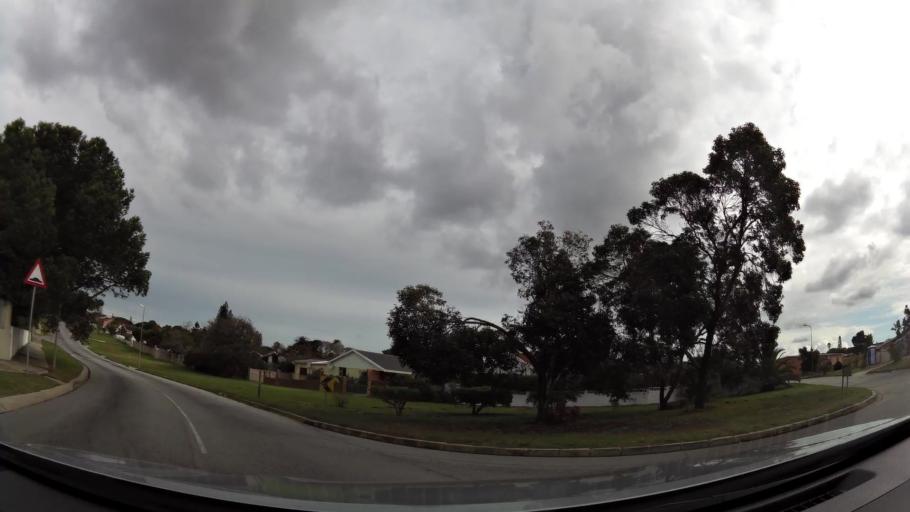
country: ZA
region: Eastern Cape
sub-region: Nelson Mandela Bay Metropolitan Municipality
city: Port Elizabeth
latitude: -33.9360
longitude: 25.5116
